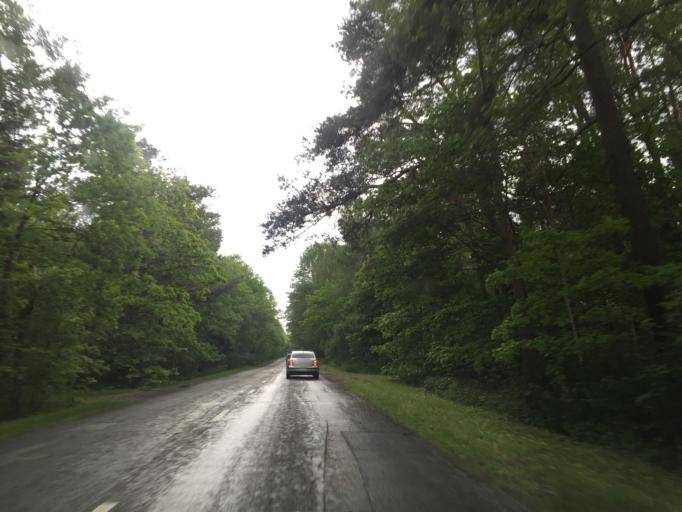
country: LT
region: Klaipedos apskritis
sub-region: Klaipeda
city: Klaipeda
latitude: 55.7416
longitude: 21.0949
